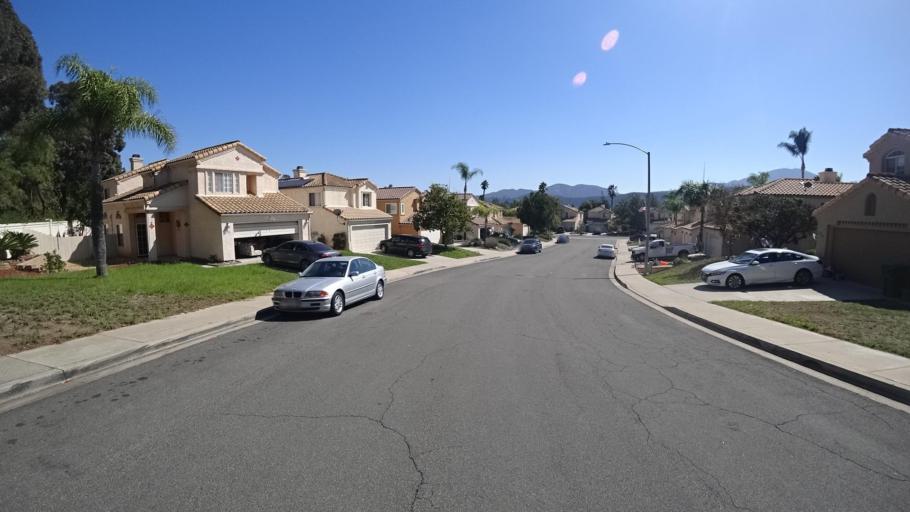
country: US
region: California
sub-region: San Diego County
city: Rancho San Diego
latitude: 32.7511
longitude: -116.9293
